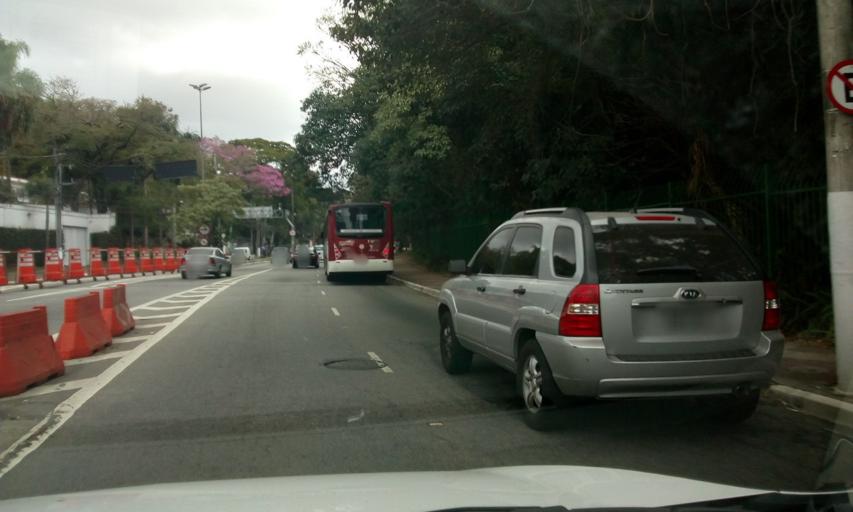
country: BR
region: Sao Paulo
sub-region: Sao Paulo
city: Sao Paulo
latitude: -23.5880
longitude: -46.6996
